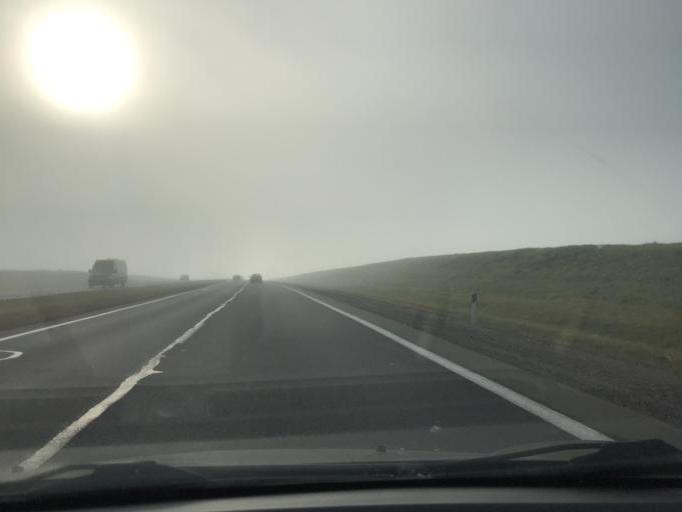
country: BY
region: Minsk
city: Luhavaya Slabada
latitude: 53.7488
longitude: 27.8344
